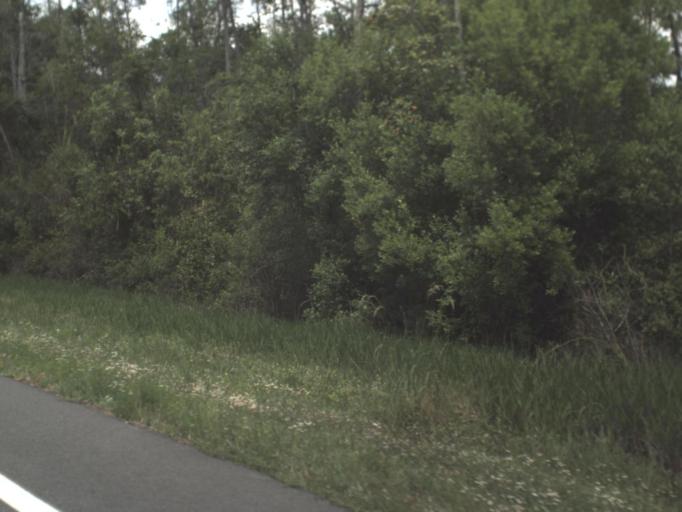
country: US
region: Florida
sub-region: Hamilton County
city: Jasper
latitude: 30.5478
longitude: -82.6801
